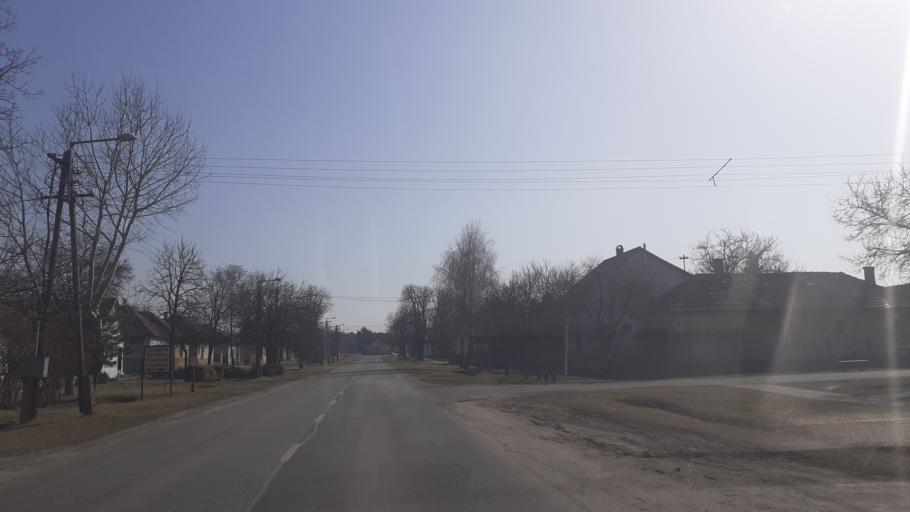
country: HU
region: Pest
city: Orkeny
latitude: 47.0802
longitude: 19.3716
